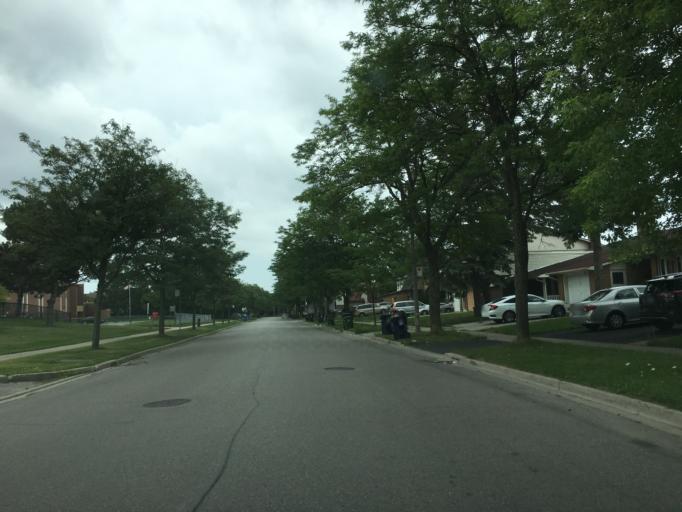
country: CA
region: Ontario
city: Scarborough
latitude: 43.8088
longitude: -79.2866
